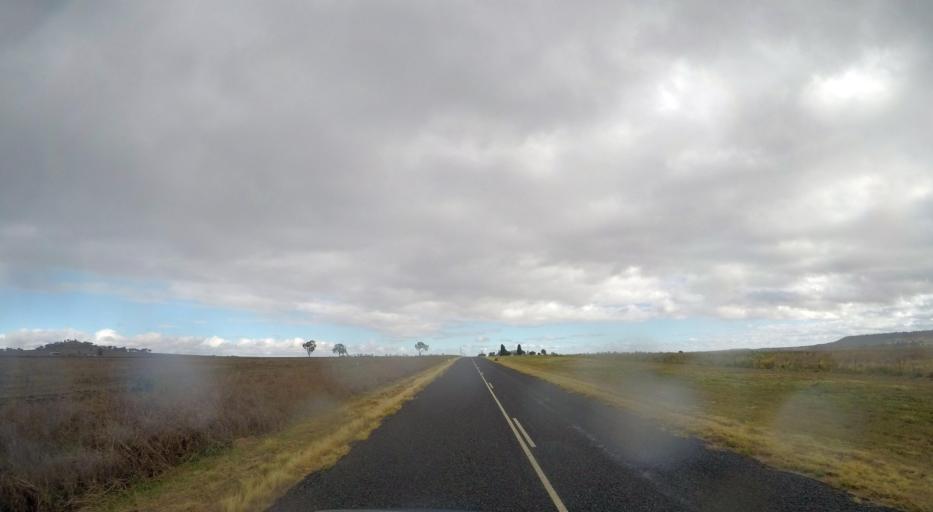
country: AU
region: Queensland
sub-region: Southern Downs
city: Warwick
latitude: -28.0499
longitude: 152.0372
